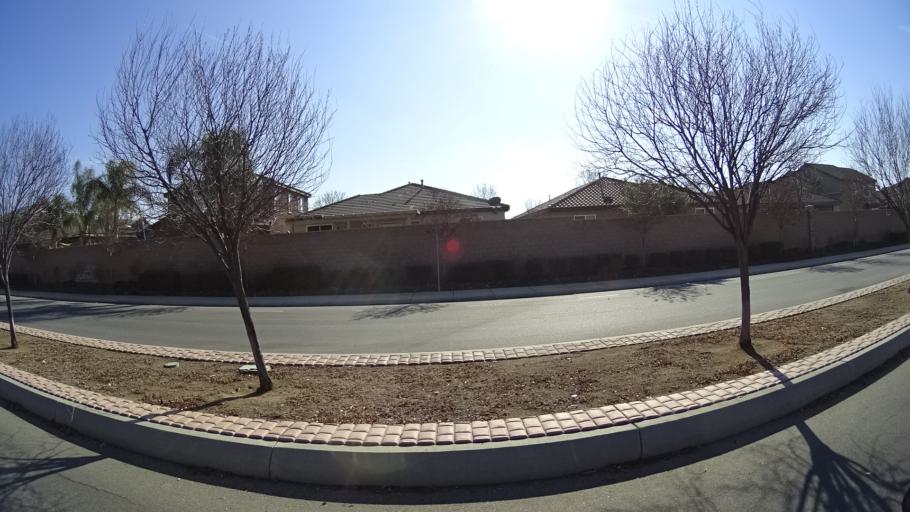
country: US
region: California
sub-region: Kern County
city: Oildale
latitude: 35.4079
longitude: -118.8909
